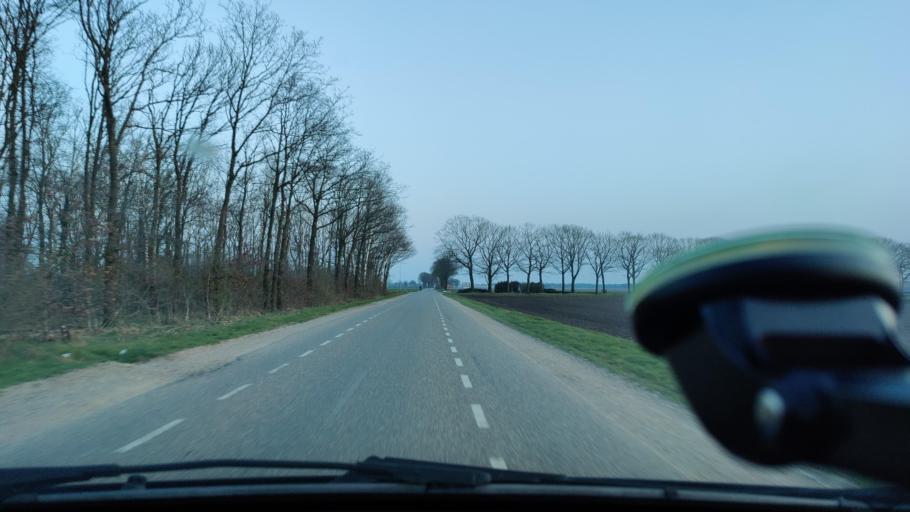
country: NL
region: Limburg
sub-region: Gemeente Bergen
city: Wellerlooi
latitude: 51.5675
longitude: 6.1444
